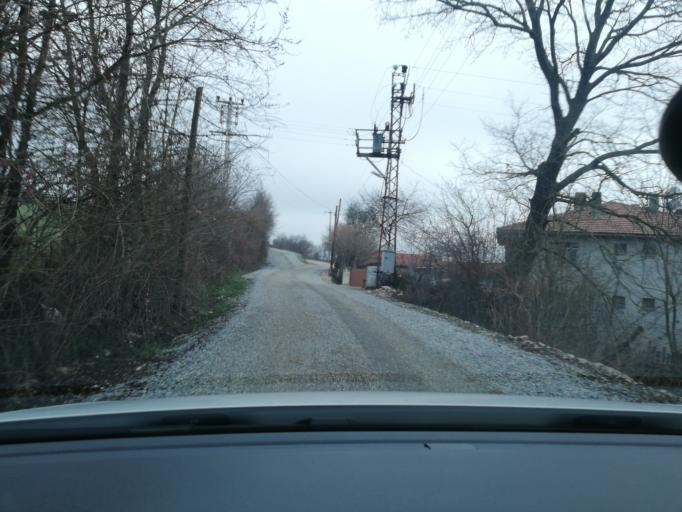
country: TR
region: Bolu
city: Bolu
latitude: 40.6651
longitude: 31.4628
